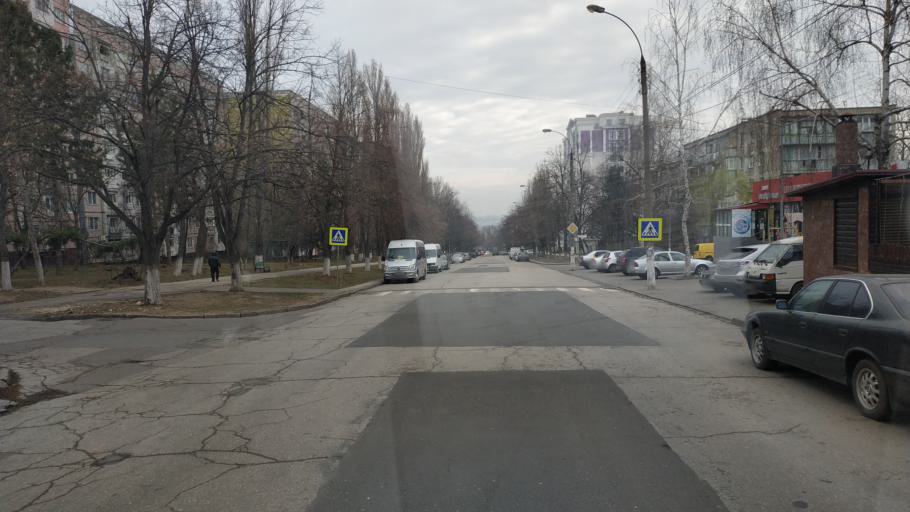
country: MD
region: Chisinau
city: Vatra
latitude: 47.0367
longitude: 28.7773
